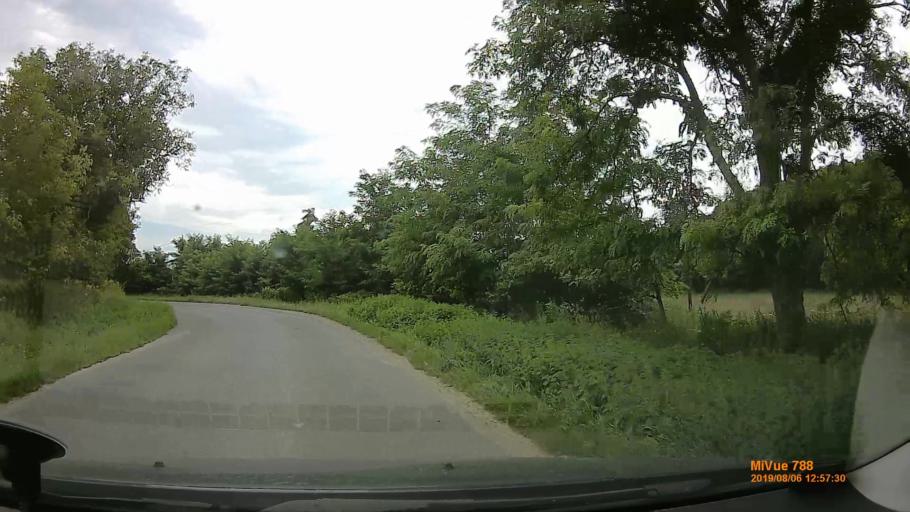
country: HU
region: Zala
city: Pacsa
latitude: 46.6311
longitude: 17.0400
